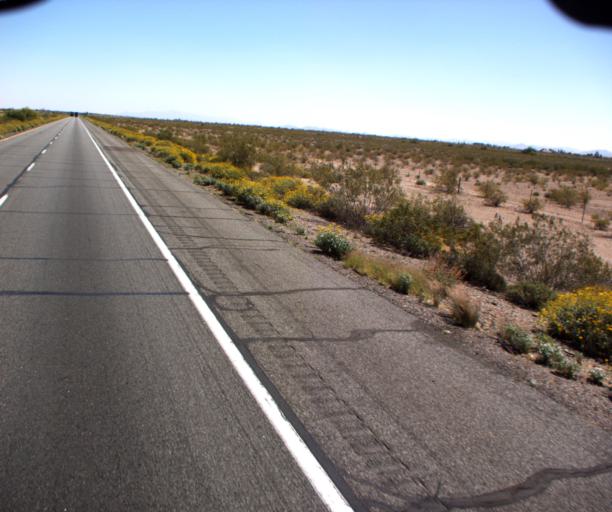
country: US
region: Arizona
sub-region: Maricopa County
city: Buckeye
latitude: 33.4735
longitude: -112.8310
